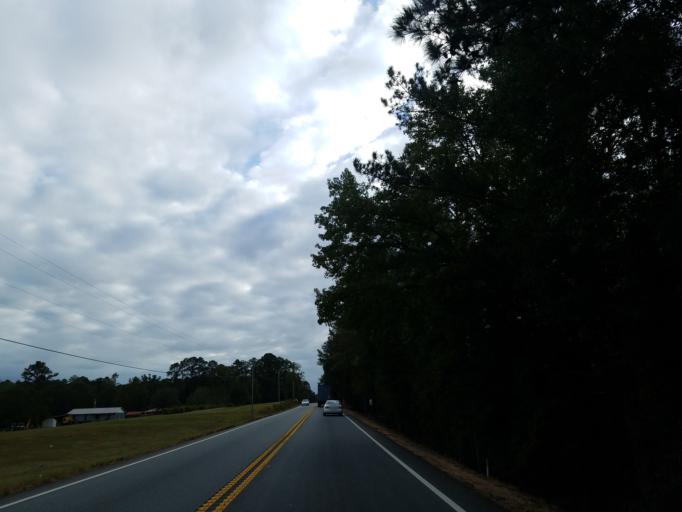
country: US
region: Georgia
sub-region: Lamar County
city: Barnesville
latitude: 33.1810
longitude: -84.0815
